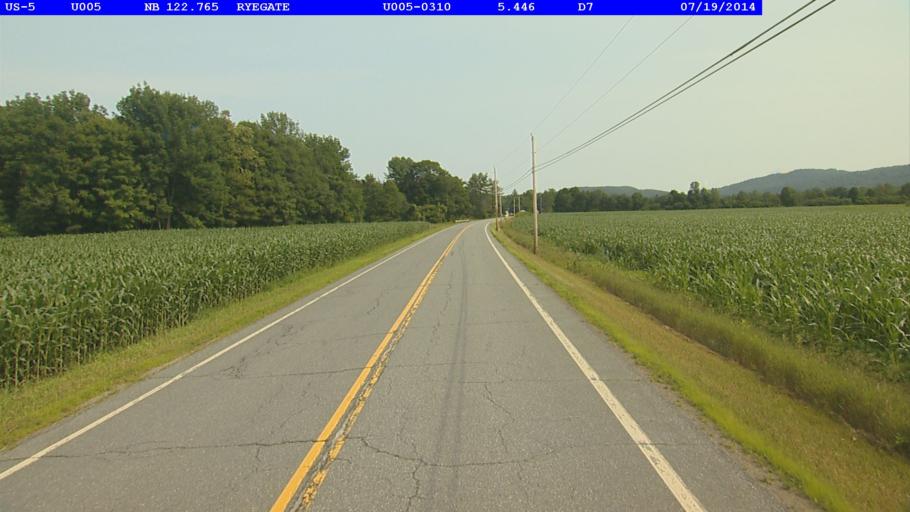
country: US
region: New Hampshire
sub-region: Grafton County
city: Woodsville
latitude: 44.2299
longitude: -72.0576
